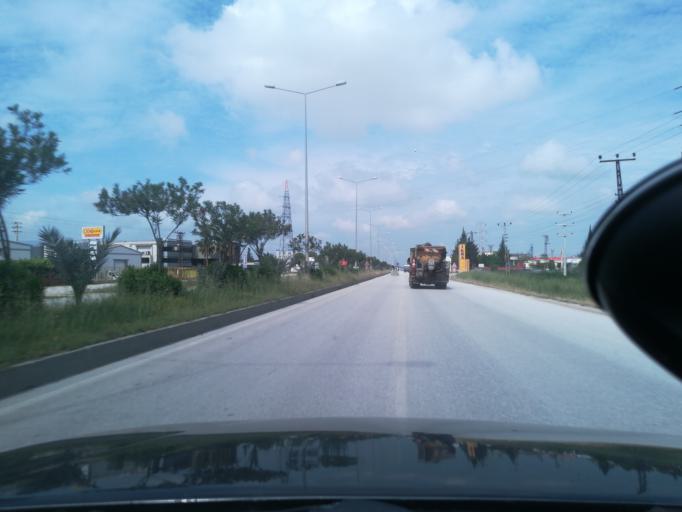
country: TR
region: Adana
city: Yuregir
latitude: 36.9829
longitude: 35.4129
